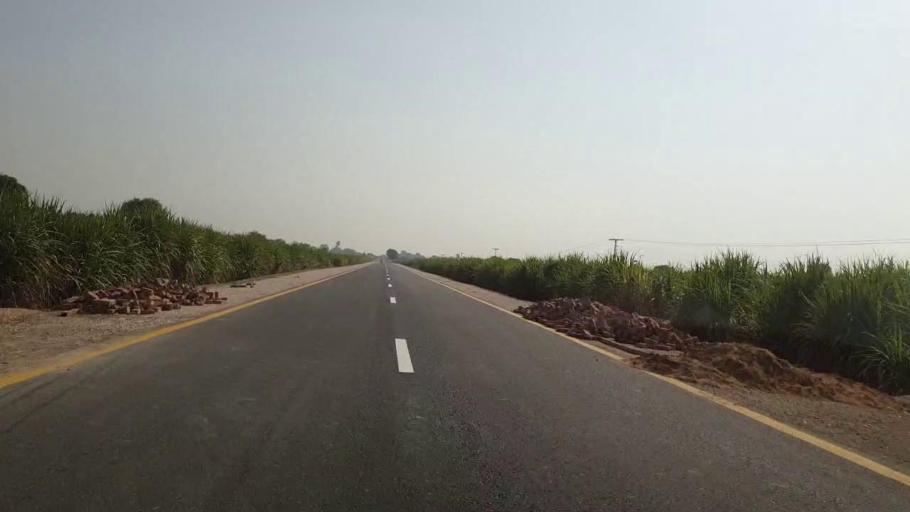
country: PK
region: Sindh
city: Bhan
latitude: 26.6105
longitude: 67.7787
